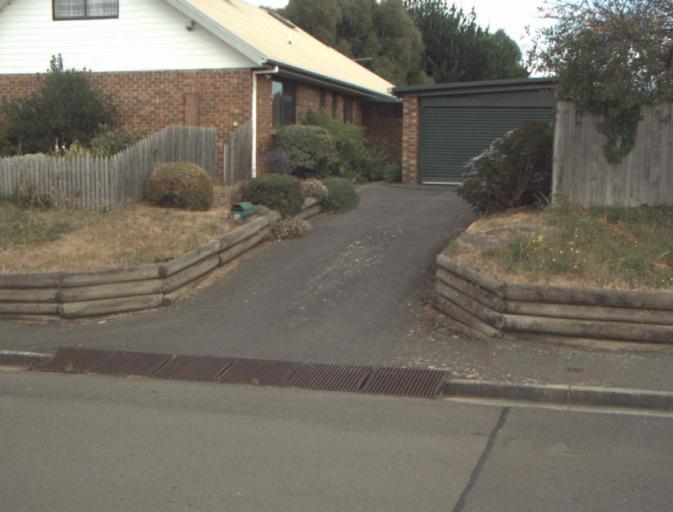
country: AU
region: Tasmania
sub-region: Launceston
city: Summerhill
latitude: -41.4832
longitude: 147.1618
